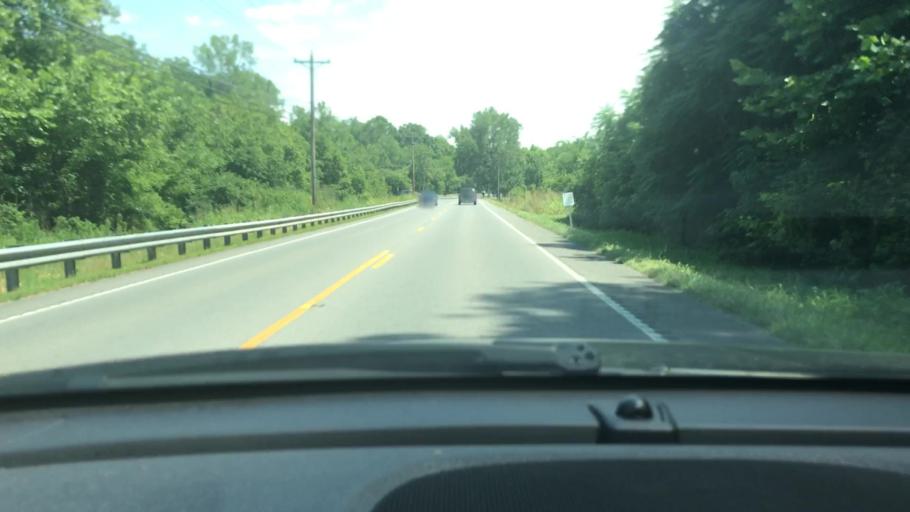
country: US
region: Tennessee
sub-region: Sumner County
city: Shackle Island
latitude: 36.3904
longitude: -86.6250
